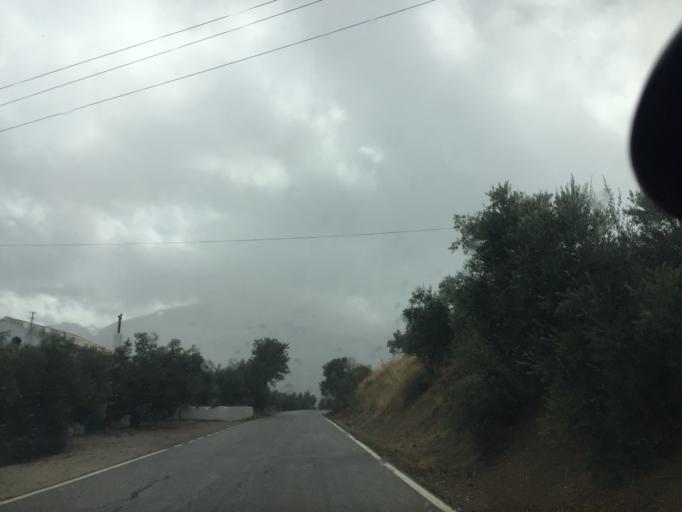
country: ES
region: Andalusia
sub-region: Provincia de Jaen
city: Jimena
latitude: 37.8126
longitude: -3.4595
